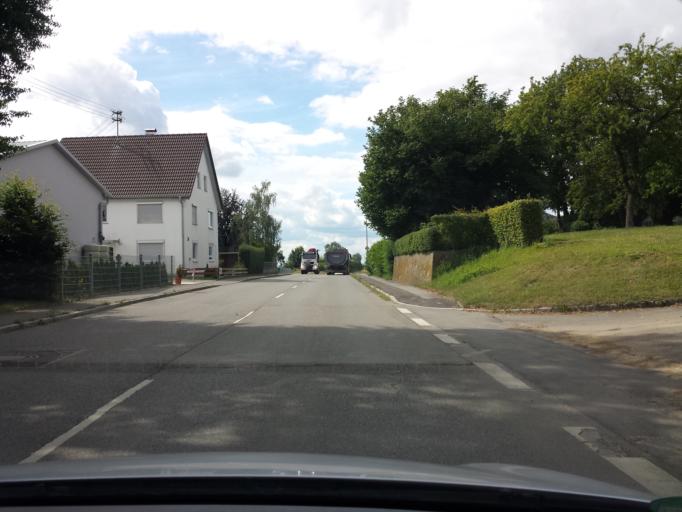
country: DE
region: Baden-Wuerttemberg
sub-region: Tuebingen Region
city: Burgrieden
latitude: 48.2284
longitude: 9.9500
